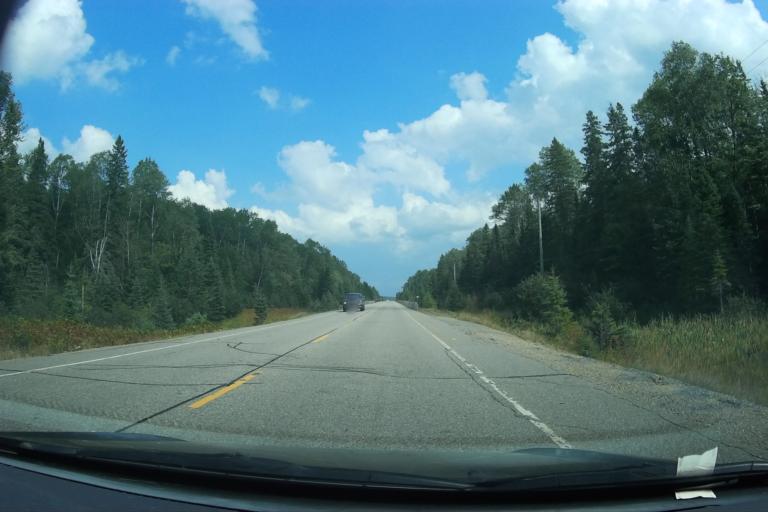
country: CA
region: Ontario
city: Bancroft
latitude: 45.5912
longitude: -78.3517
